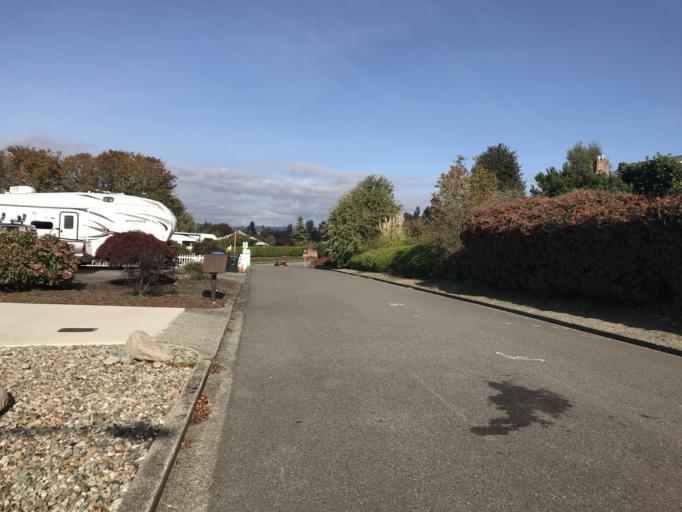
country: US
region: Washington
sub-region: Pierce County
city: University Place
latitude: 47.2518
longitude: -122.5423
